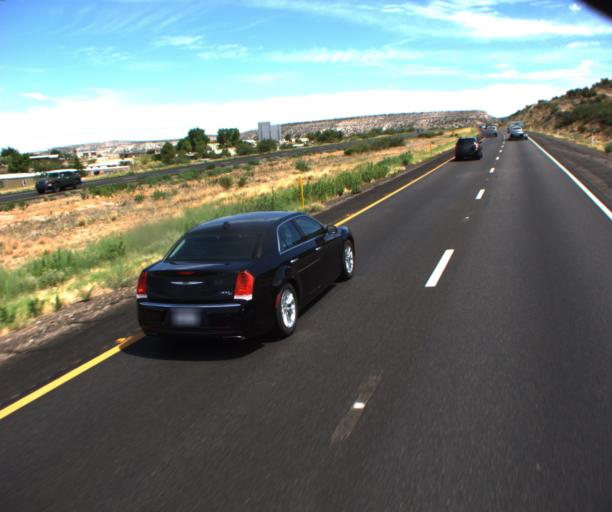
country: US
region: Arizona
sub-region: Yavapai County
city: Camp Verde
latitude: 34.6007
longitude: -111.8717
